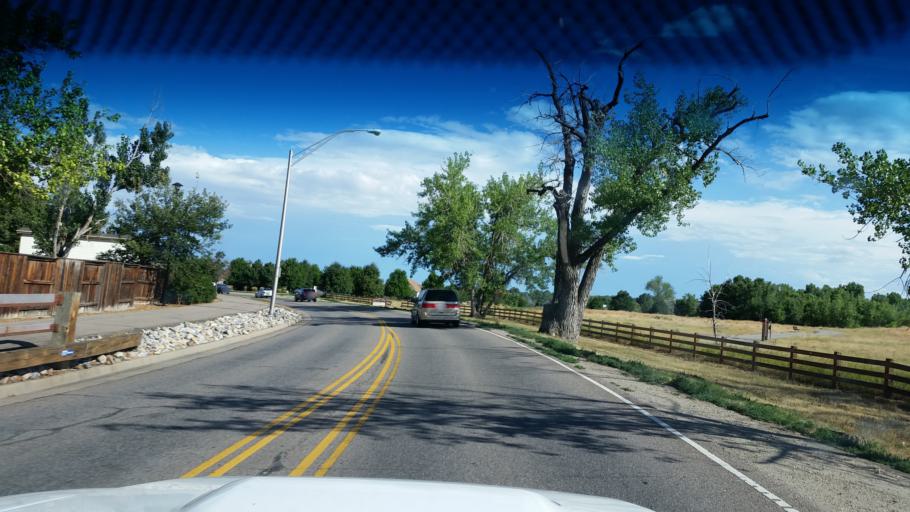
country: US
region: Colorado
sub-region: Adams County
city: Northglenn
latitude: 39.9279
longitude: -104.9485
